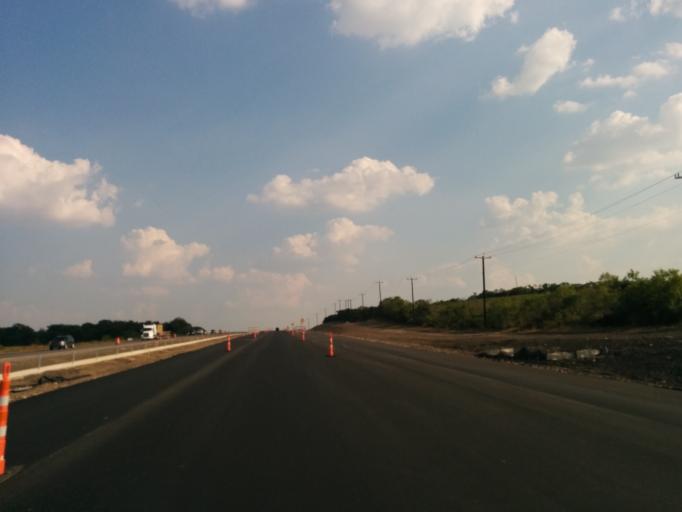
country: US
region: Texas
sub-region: Bexar County
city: Converse
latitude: 29.4746
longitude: -98.2951
